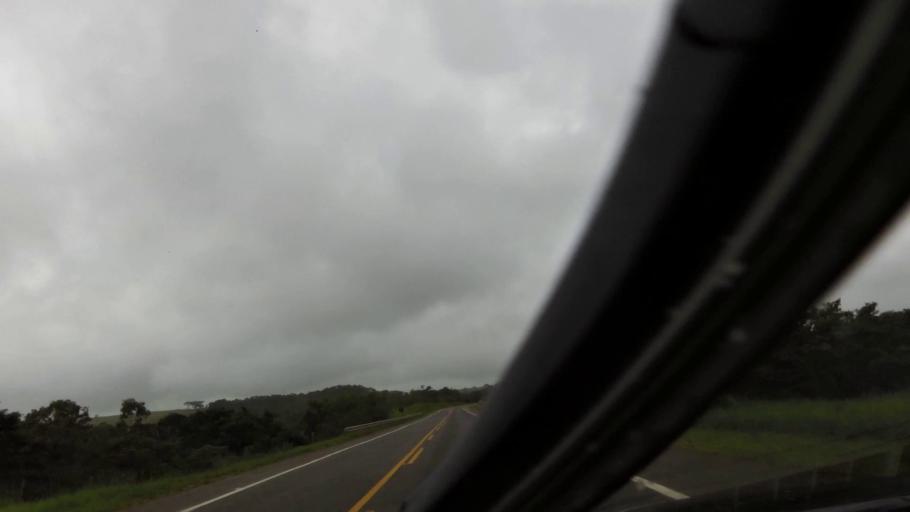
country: BR
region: Espirito Santo
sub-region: Guarapari
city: Guarapari
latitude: -20.7125
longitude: -40.5762
